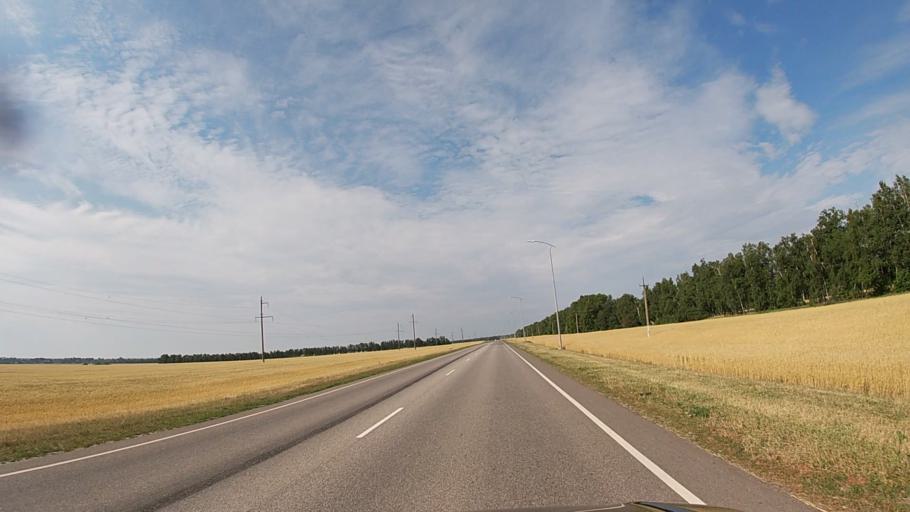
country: RU
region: Belgorod
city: Proletarskiy
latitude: 50.8190
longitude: 35.7551
